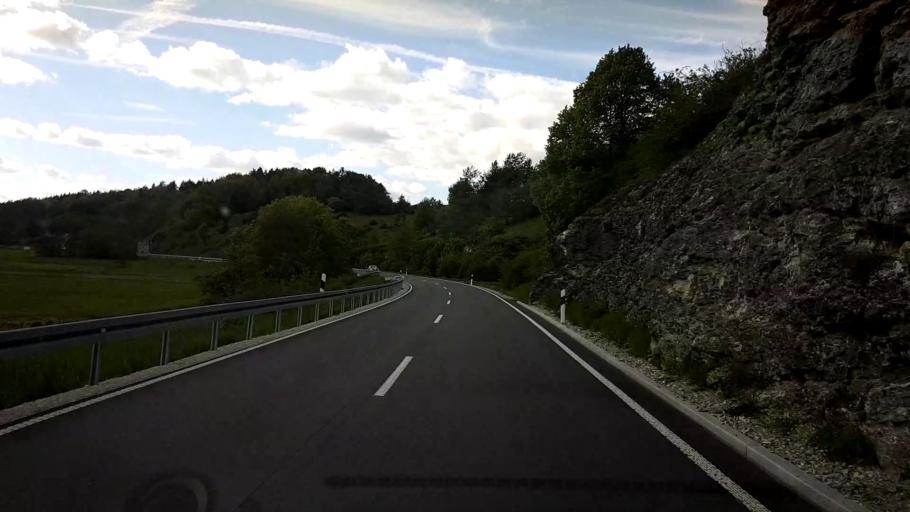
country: DE
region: Bavaria
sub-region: Upper Franconia
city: Hollfeld
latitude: 49.9510
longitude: 11.2777
